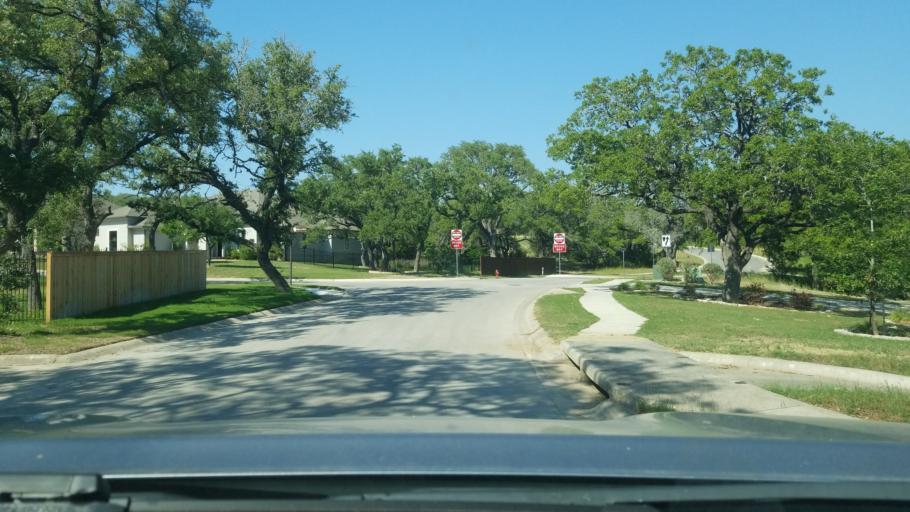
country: US
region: Texas
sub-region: Comal County
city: Bulverde
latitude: 29.7604
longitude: -98.4194
